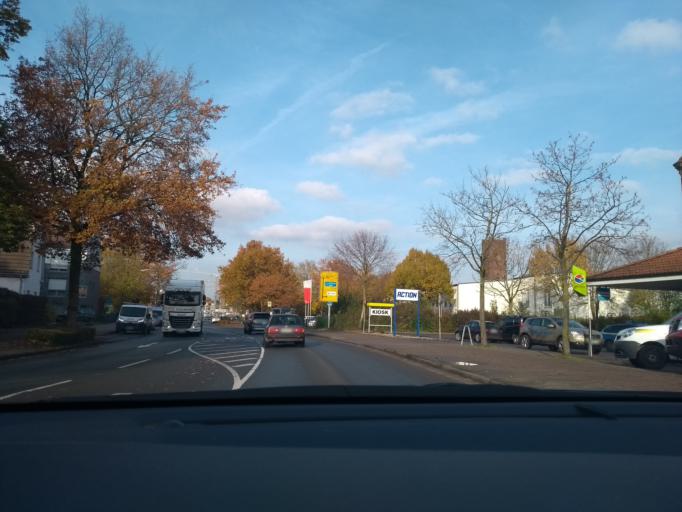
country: DE
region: North Rhine-Westphalia
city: Selm
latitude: 51.6925
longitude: 7.4672
